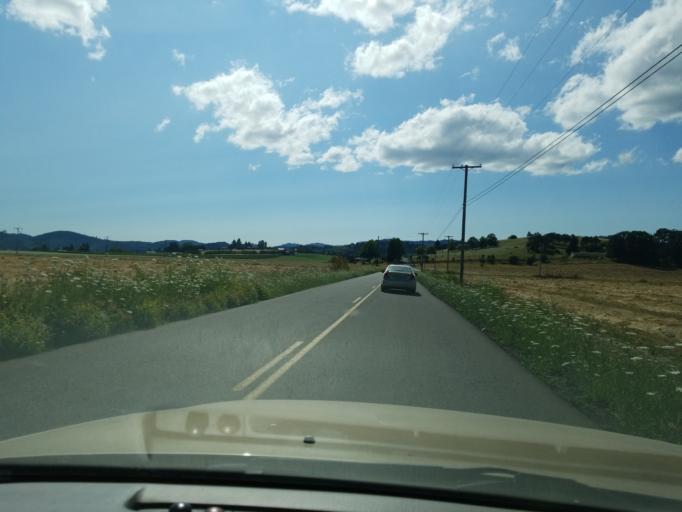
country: US
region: Oregon
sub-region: Yamhill County
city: McMinnville
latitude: 45.2450
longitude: -123.2129
